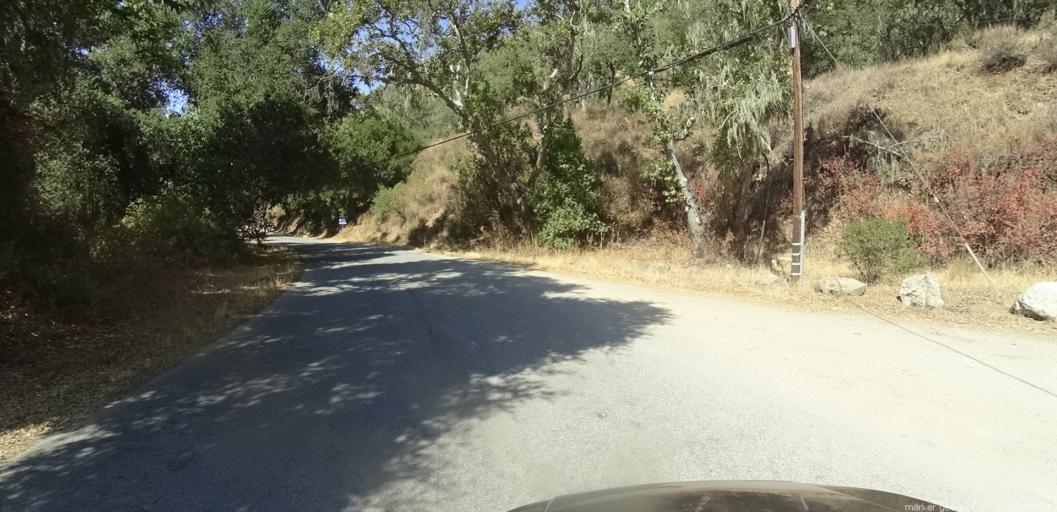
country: US
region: California
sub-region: Monterey County
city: Carmel Valley Village
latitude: 36.3922
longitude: -121.6258
